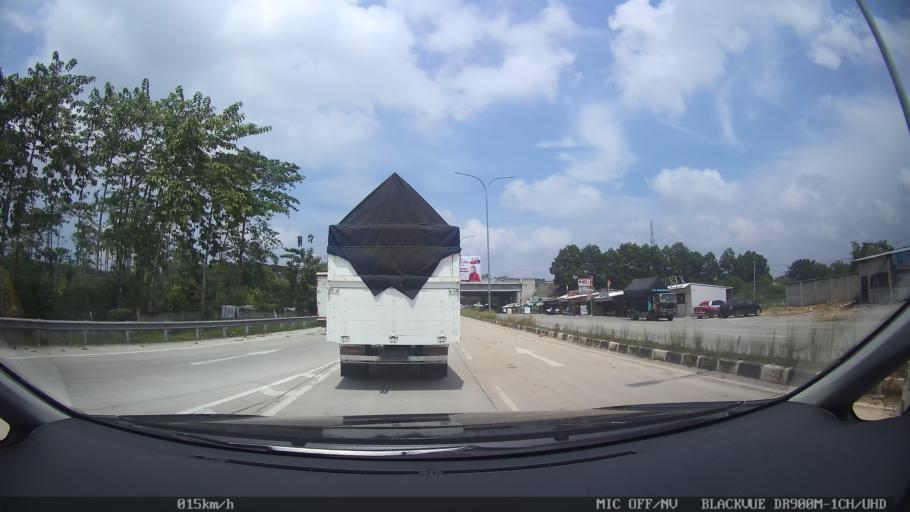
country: ID
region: Lampung
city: Kedaton
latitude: -5.3525
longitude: 105.3241
